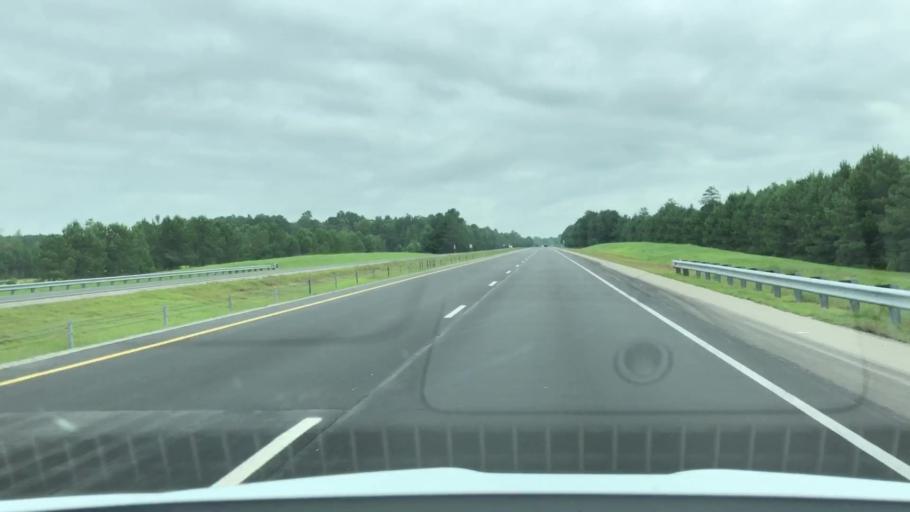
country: US
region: North Carolina
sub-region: Wilson County
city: Lucama
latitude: 35.6072
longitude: -77.9801
